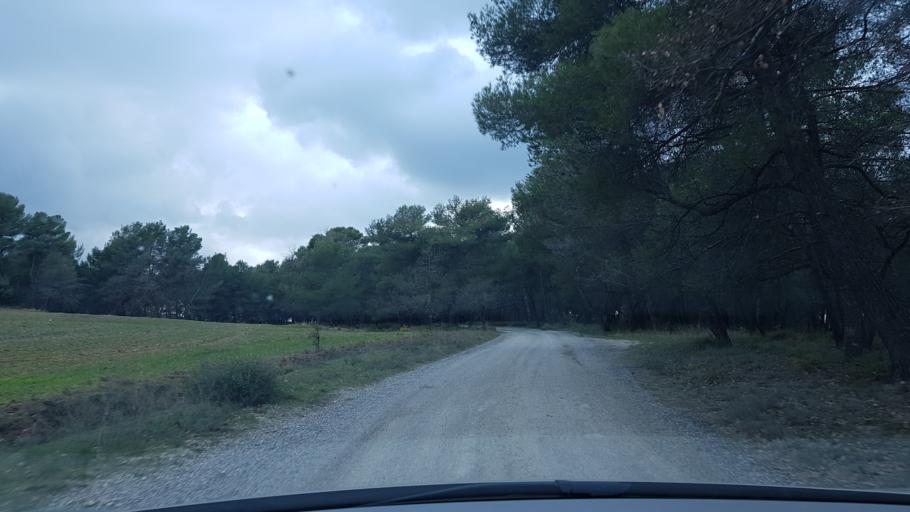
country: FR
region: Provence-Alpes-Cote d'Azur
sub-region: Departement des Bouches-du-Rhone
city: Mimet
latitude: 43.4252
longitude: 5.5178
